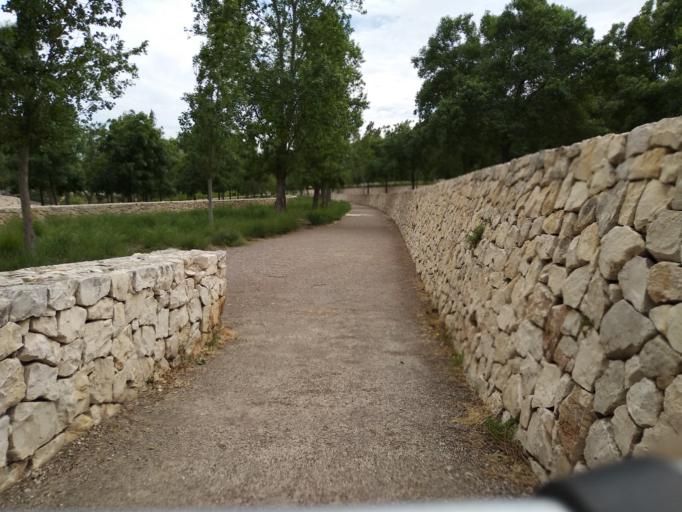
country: ES
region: Valencia
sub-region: Provincia de Valencia
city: Mislata
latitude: 39.4796
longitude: -0.4096
